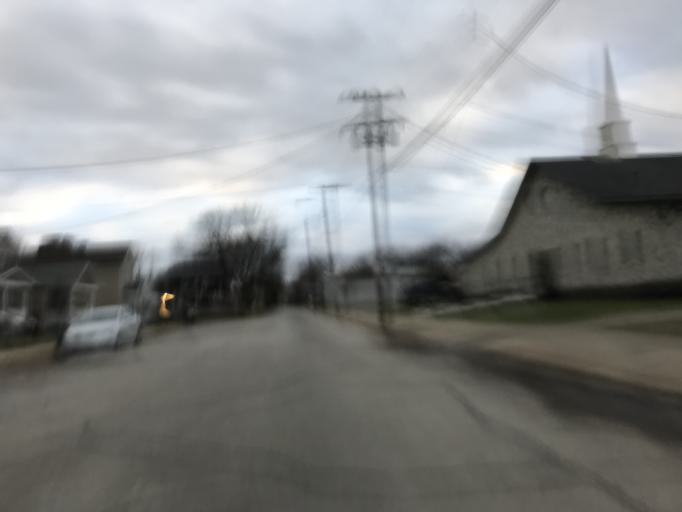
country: US
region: Kentucky
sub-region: Jefferson County
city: Louisville
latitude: 38.2364
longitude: -85.7451
